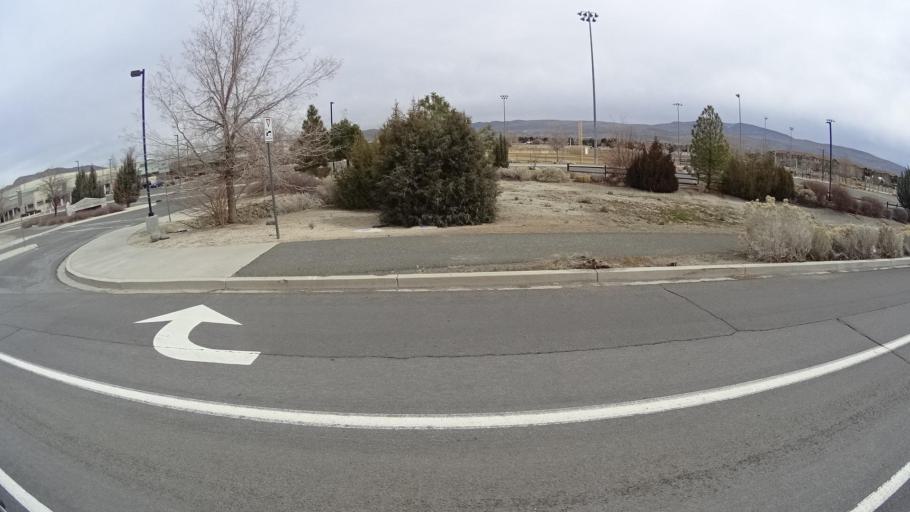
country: US
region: Nevada
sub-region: Washoe County
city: Spanish Springs
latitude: 39.6460
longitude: -119.7233
